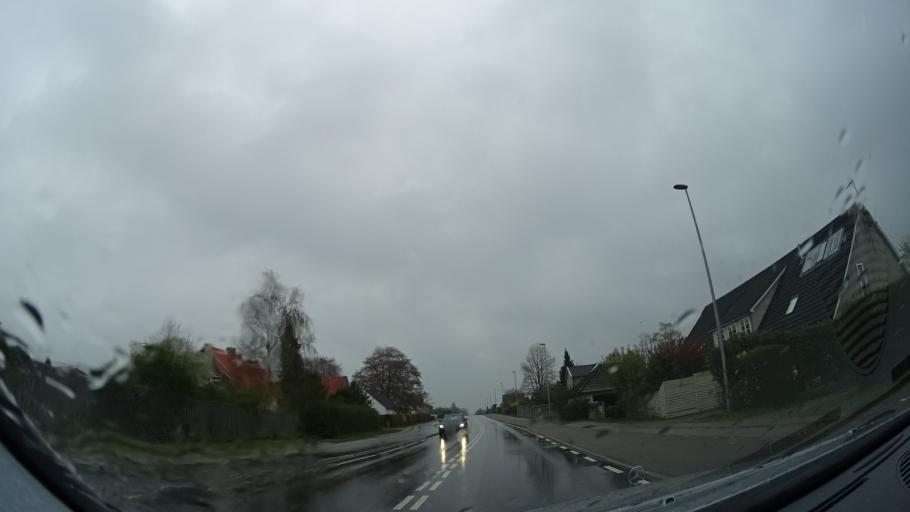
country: DK
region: Zealand
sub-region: Holbaek Kommune
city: Holbaek
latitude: 55.7147
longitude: 11.6786
